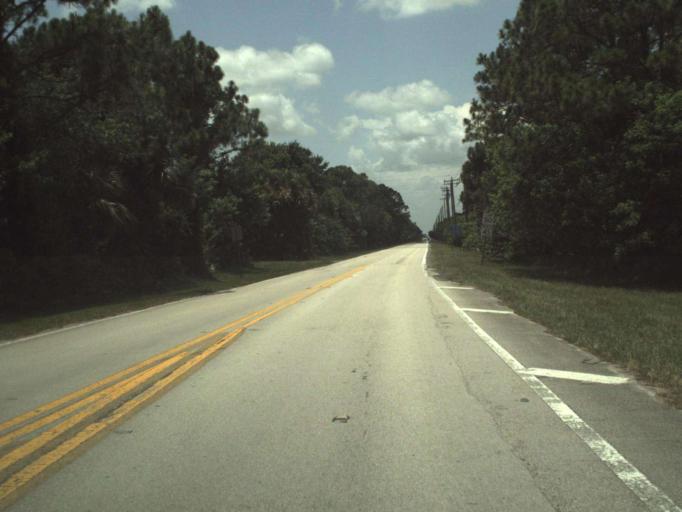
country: US
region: Florida
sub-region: Saint Lucie County
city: Fort Pierce South
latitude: 27.3744
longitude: -80.4210
